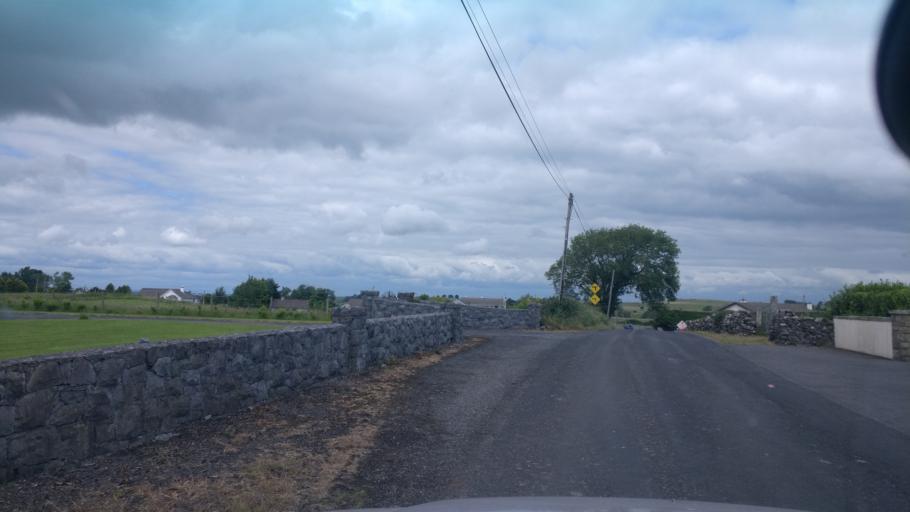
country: IE
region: Connaught
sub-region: County Galway
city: Loughrea
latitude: 53.1686
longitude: -8.5534
